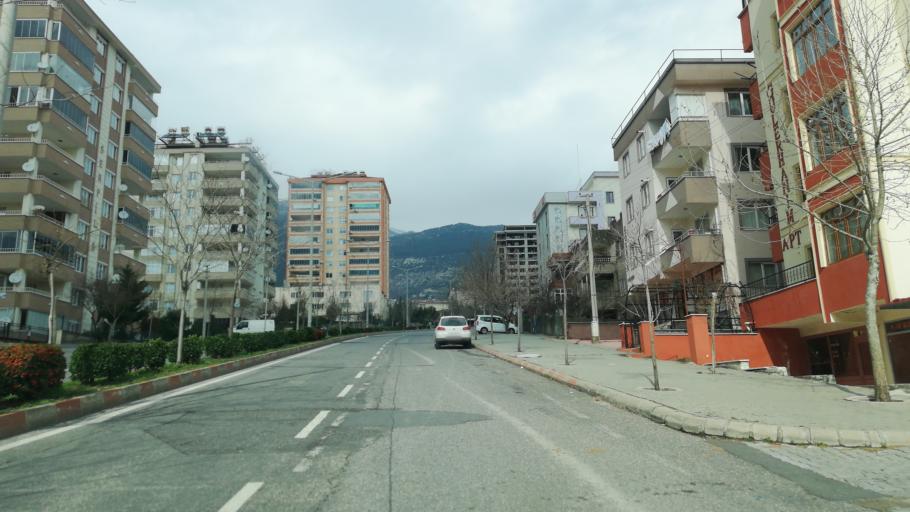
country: TR
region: Kahramanmaras
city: Kahramanmaras
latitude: 37.5904
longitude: 36.8634
